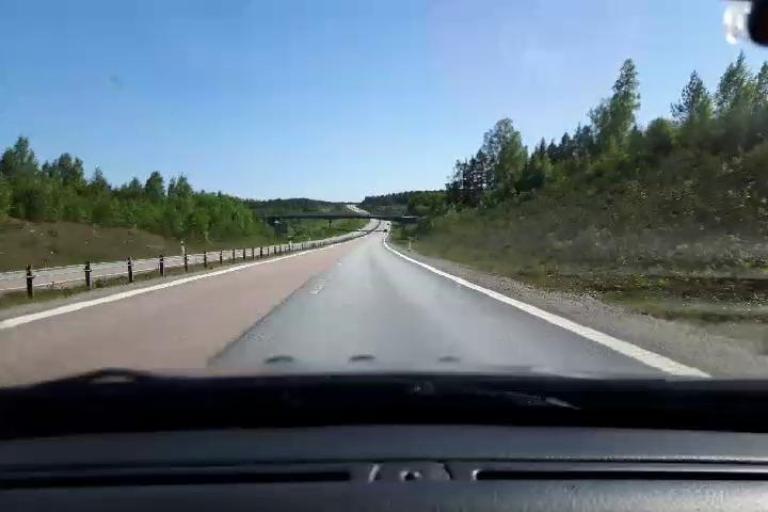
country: SE
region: Gaevleborg
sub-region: Soderhamns Kommun
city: Soderhamn
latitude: 61.3604
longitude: 17.0140
